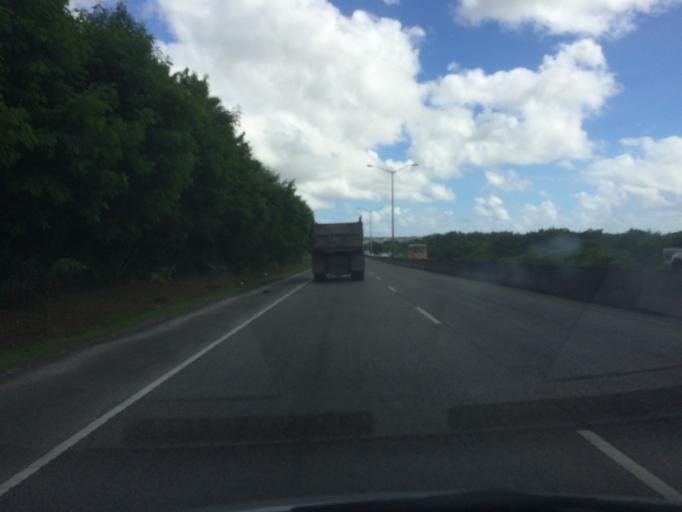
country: BB
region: Saint Michael
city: Bridgetown
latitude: 13.1310
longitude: -59.5992
